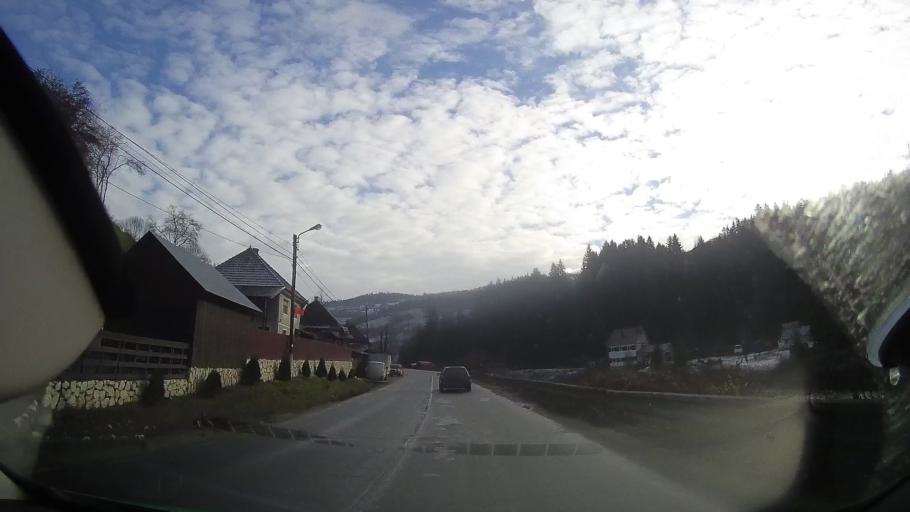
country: RO
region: Alba
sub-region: Oras Campeni
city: Campeni
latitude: 46.3599
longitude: 23.0653
